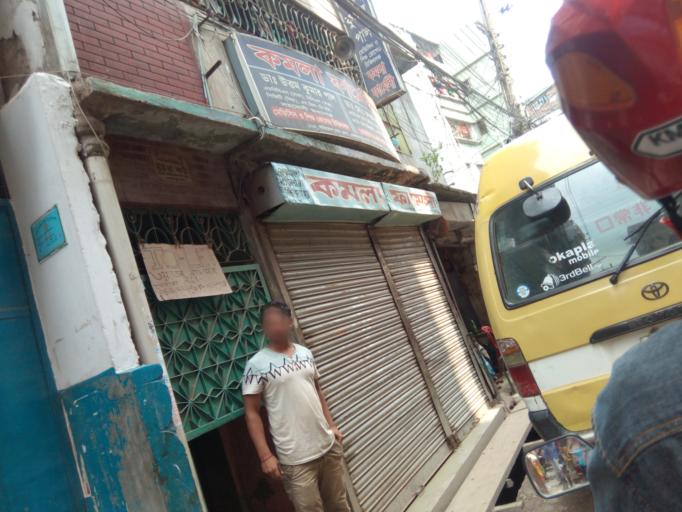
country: BD
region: Dhaka
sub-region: Dhaka
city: Dhaka
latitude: 23.7072
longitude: 90.4179
